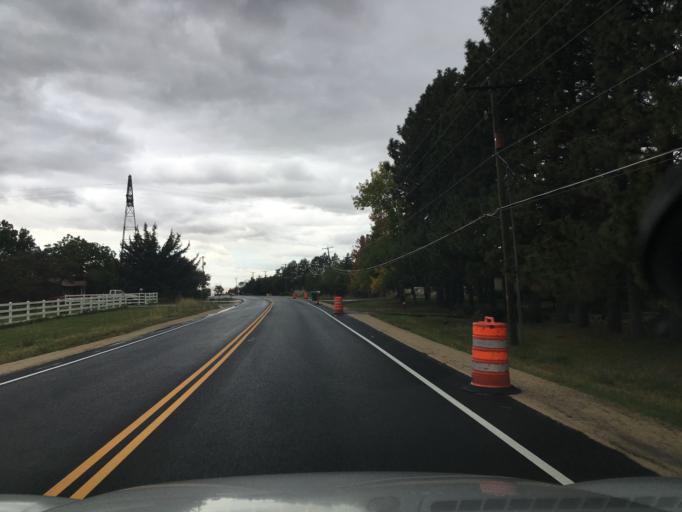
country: US
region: Utah
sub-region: Davis County
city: Fruit Heights
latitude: 41.0661
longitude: -111.9143
